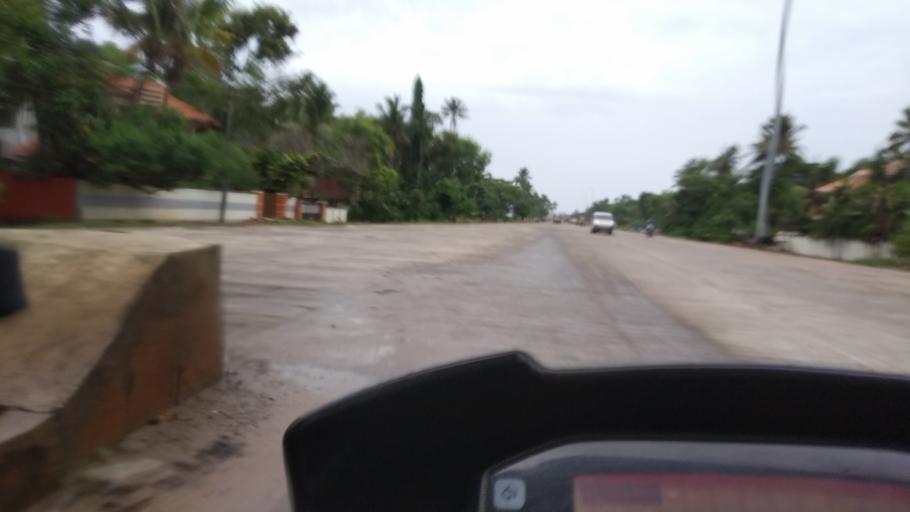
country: IN
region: Kerala
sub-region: Alappuzha
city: Alleppey
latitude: 9.5118
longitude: 76.3264
